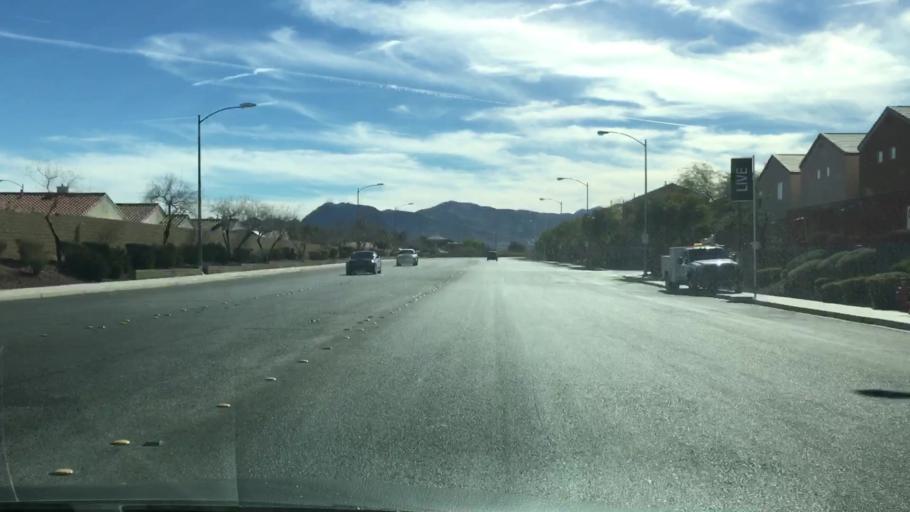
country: US
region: Nevada
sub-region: Clark County
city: Henderson
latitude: 36.0803
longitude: -115.0205
